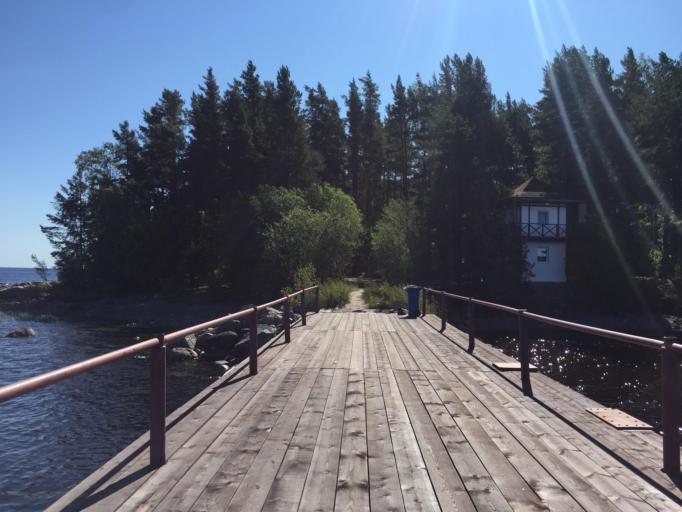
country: RU
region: Leningrad
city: Priozersk
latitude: 60.9753
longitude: 30.3078
